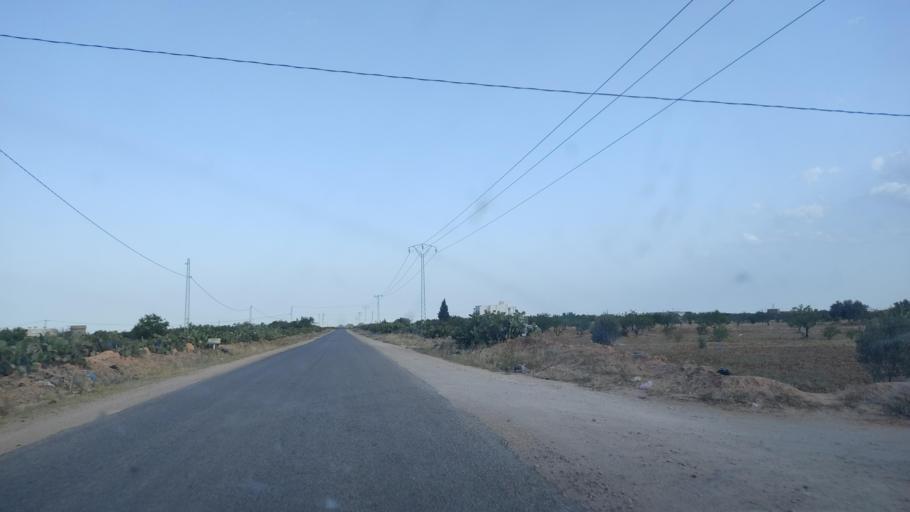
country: TN
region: Safaqis
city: Sfax
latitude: 34.8215
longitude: 10.6480
